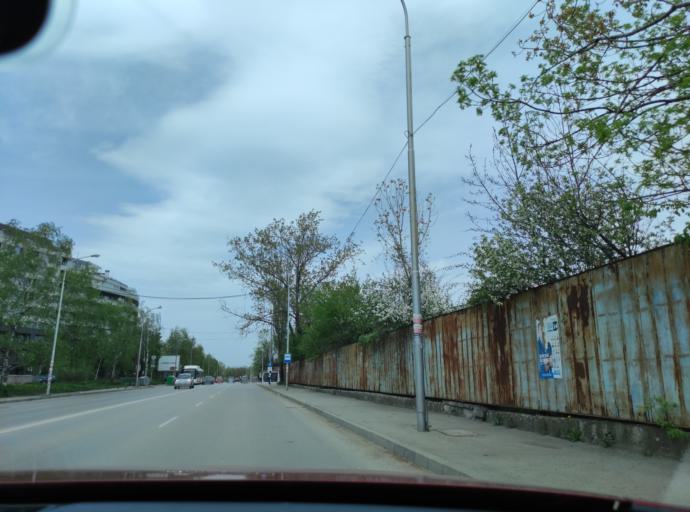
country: BG
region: Sofia-Capital
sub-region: Stolichna Obshtina
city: Sofia
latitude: 42.6485
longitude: 23.3461
